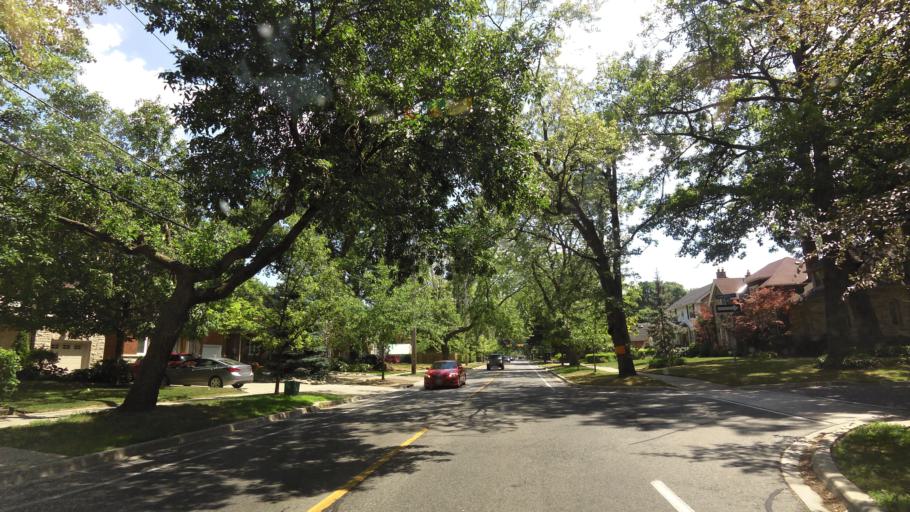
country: CA
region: Ontario
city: Etobicoke
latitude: 43.6516
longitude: -79.5132
